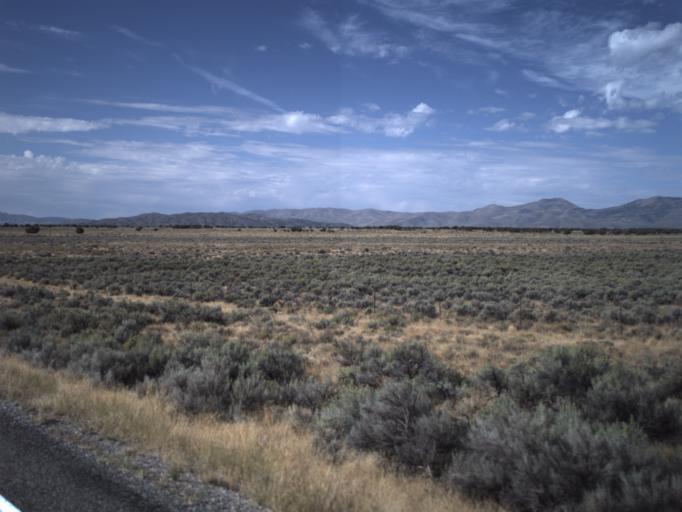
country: US
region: Idaho
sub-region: Cassia County
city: Burley
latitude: 41.7287
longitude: -113.5237
